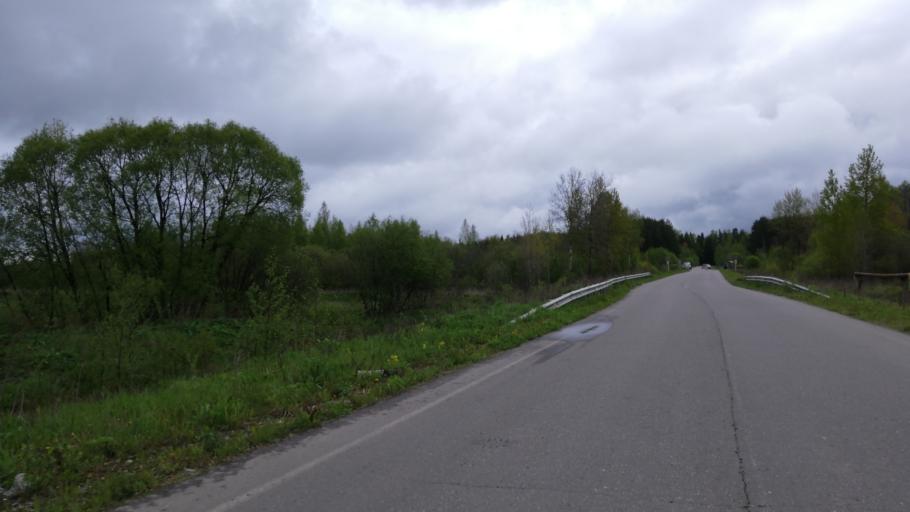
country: RU
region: Ivanovo
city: Novo-Talitsy
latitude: 57.0185
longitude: 40.7662
